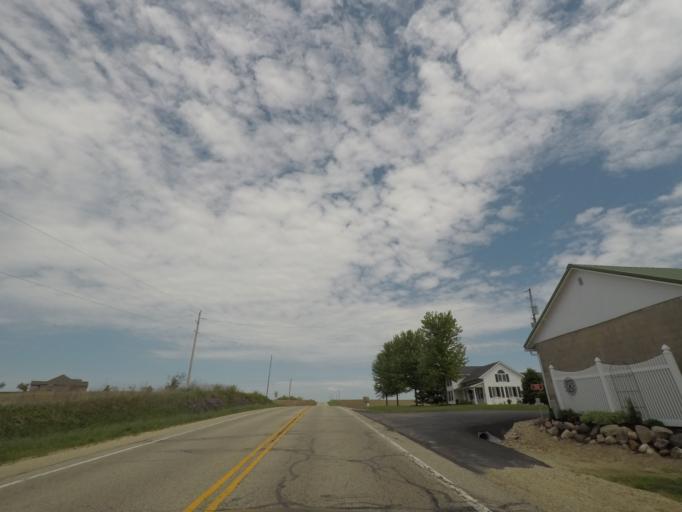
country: US
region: Wisconsin
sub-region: Rock County
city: Orfordville
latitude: 42.6894
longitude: -89.2883
